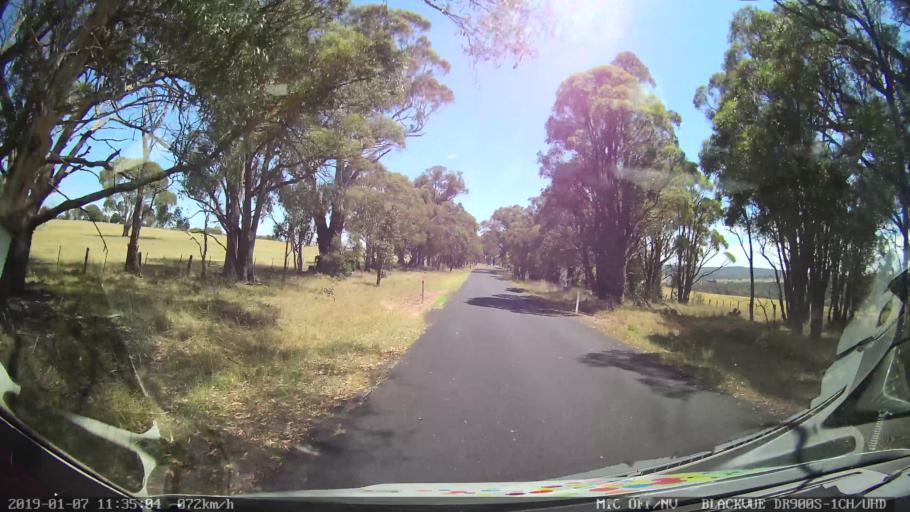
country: AU
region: New South Wales
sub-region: Armidale Dumaresq
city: Armidale
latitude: -30.3838
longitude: 151.5575
